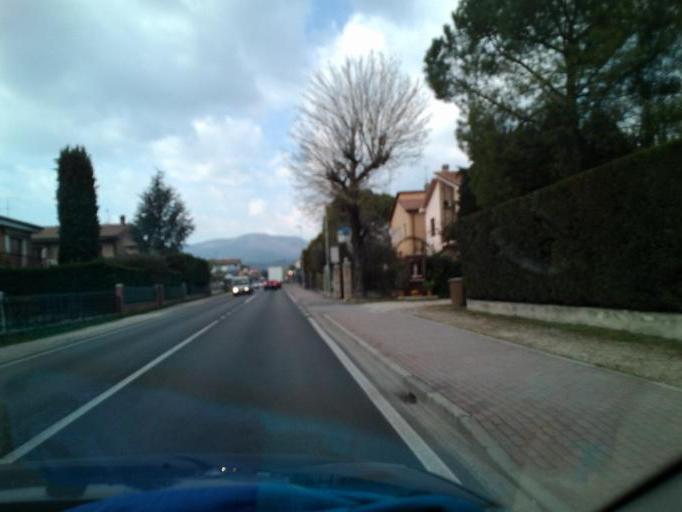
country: IT
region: Veneto
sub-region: Provincia di Verona
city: Pedemonte
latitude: 45.5033
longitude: 10.9170
